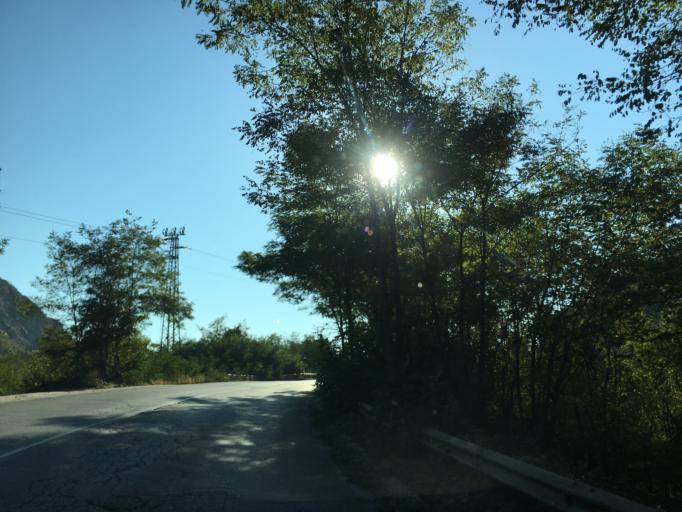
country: BG
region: Pazardzhik
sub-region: Obshtina Belovo
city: Belovo
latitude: 42.2466
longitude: 23.9272
